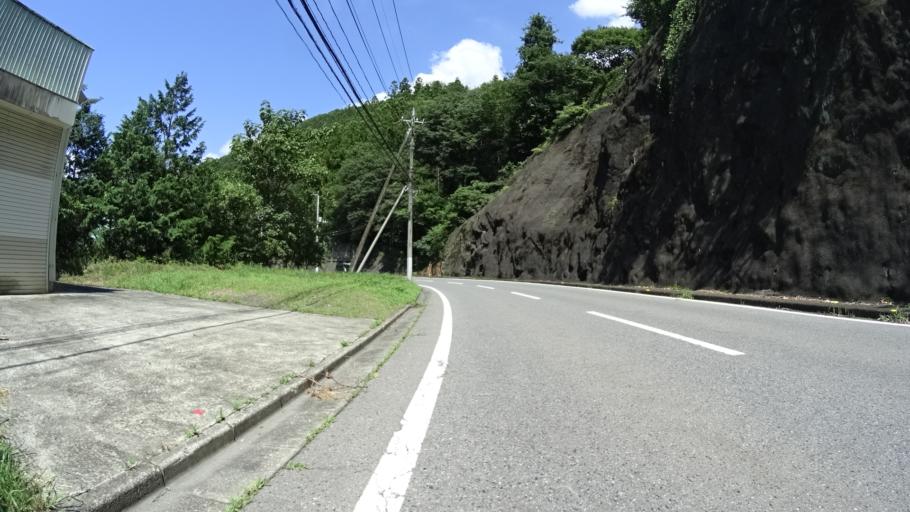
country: JP
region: Gunma
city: Tomioka
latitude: 36.0922
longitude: 138.8232
